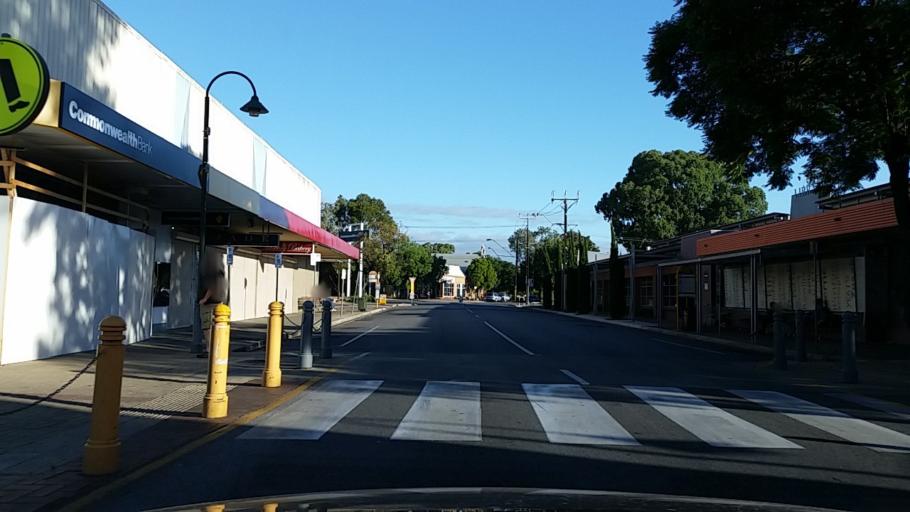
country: AU
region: South Australia
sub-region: Salisbury
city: Salisbury
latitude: -34.7624
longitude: 138.6454
